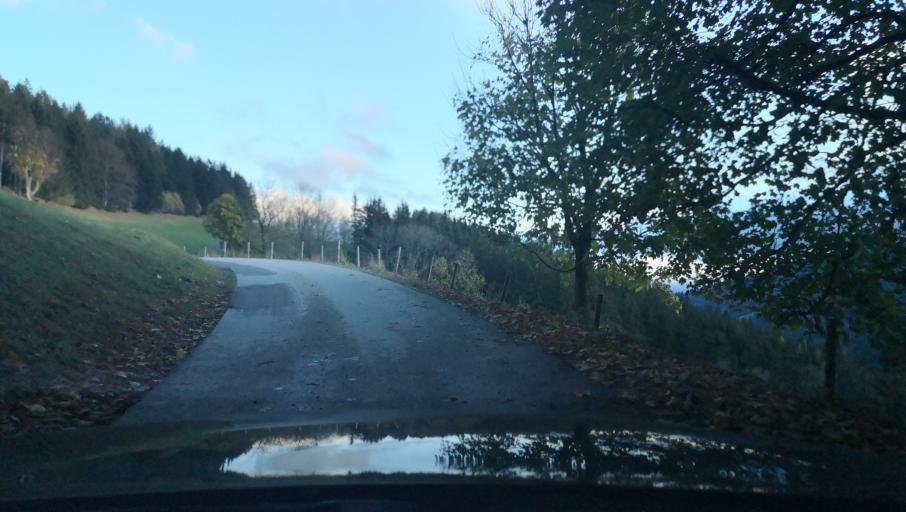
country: AT
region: Styria
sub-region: Politischer Bezirk Weiz
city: Birkfeld
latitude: 47.3340
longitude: 15.6396
